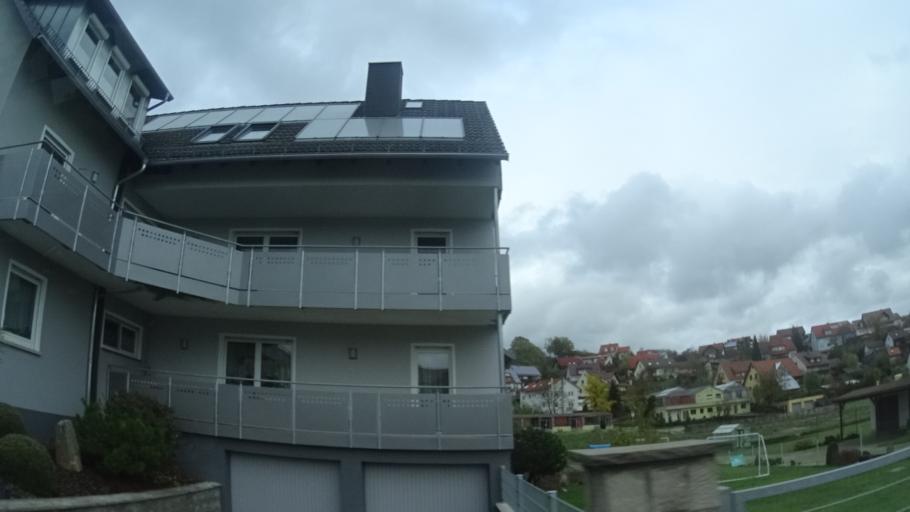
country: DE
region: Bavaria
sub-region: Regierungsbezirk Unterfranken
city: Hohenroth
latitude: 50.3355
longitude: 10.1438
